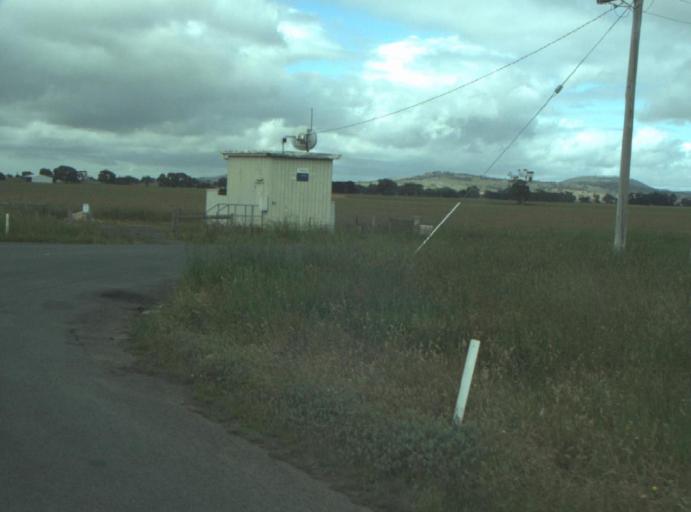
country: AU
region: Victoria
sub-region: Moorabool
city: Bacchus Marsh
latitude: -37.8339
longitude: 144.3567
